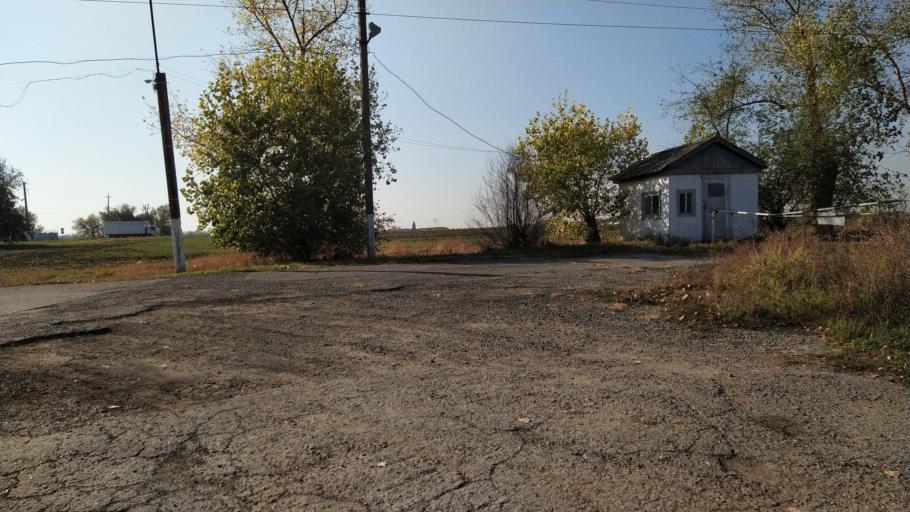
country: RU
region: Rostov
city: Bataysk
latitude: 47.0893
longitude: 39.7765
